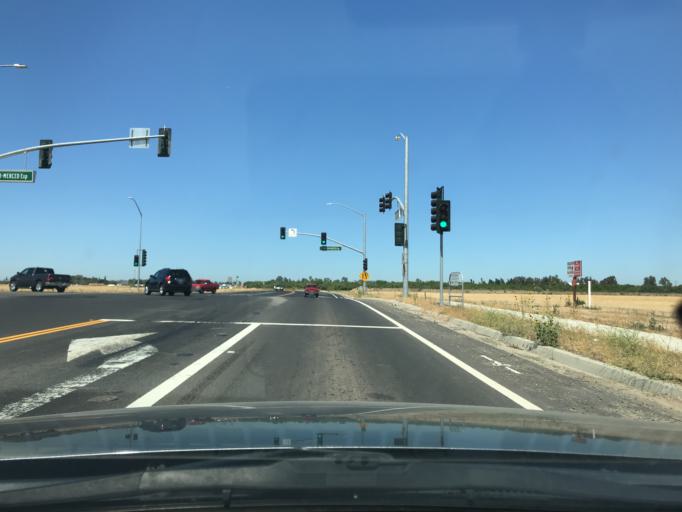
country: US
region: California
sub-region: Merced County
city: Atwater
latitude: 37.3387
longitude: -120.5638
